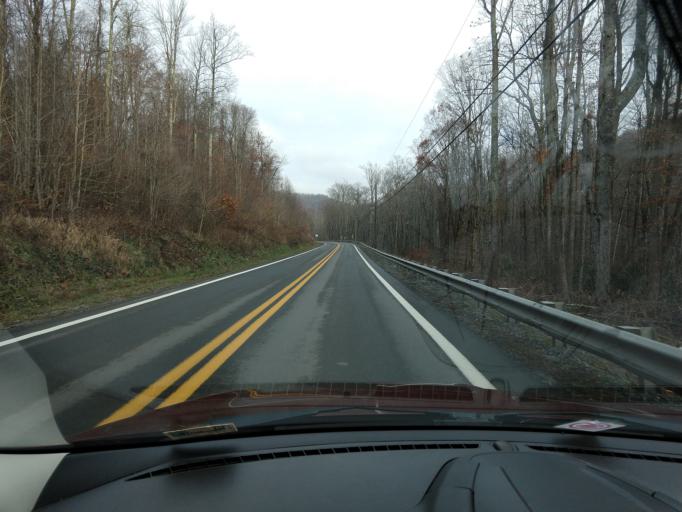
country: US
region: West Virginia
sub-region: Greenbrier County
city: Rainelle
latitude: 38.0792
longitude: -80.7079
